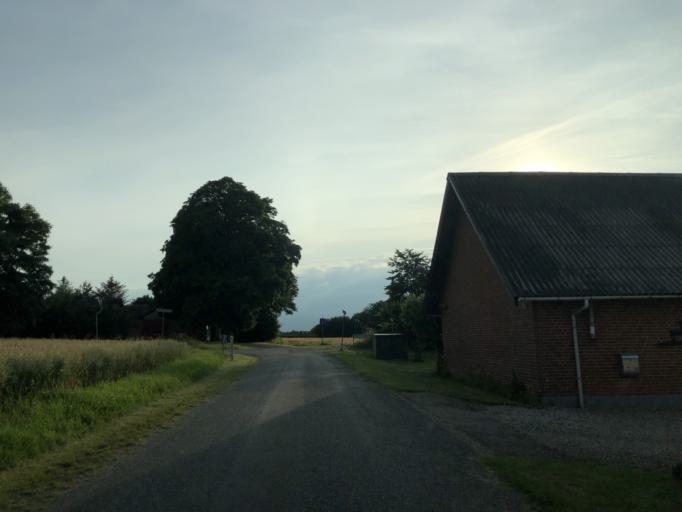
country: DK
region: South Denmark
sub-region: Fredericia Kommune
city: Taulov
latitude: 55.5868
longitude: 9.6149
